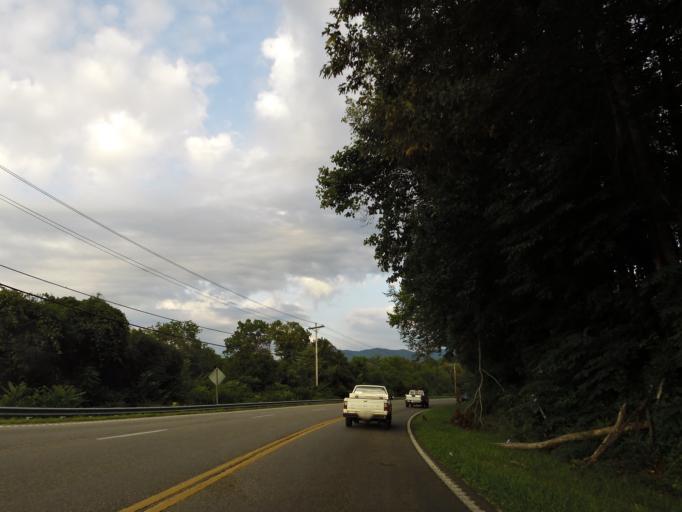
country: US
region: Tennessee
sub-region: Cocke County
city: Newport
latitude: 35.9558
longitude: -83.1476
